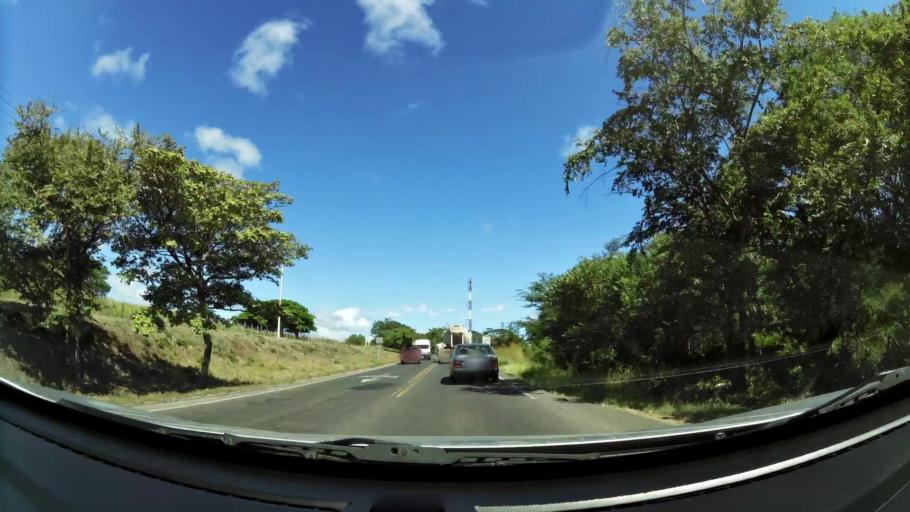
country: CR
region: Guanacaste
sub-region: Canton de Canas
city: Canas
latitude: 10.3926
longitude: -85.0804
